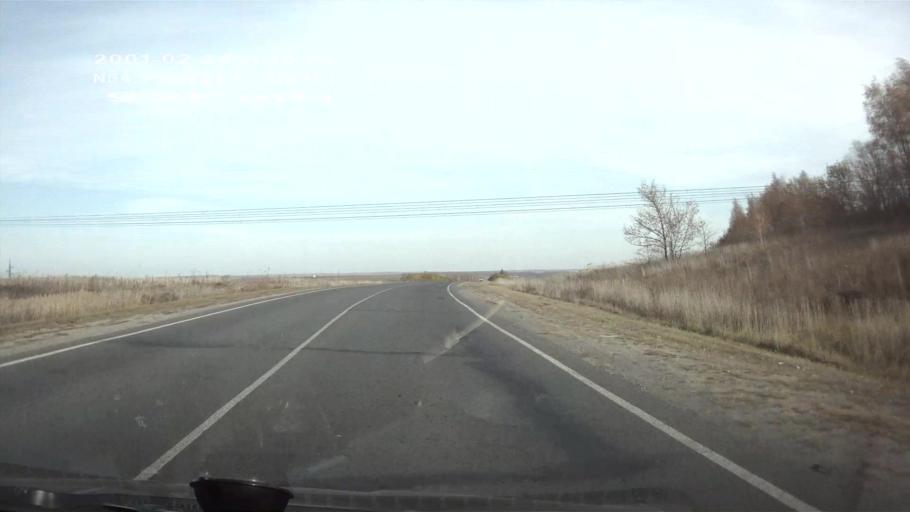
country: RU
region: Mordoviya
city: Atyashevo
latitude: 54.5382
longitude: 45.9281
